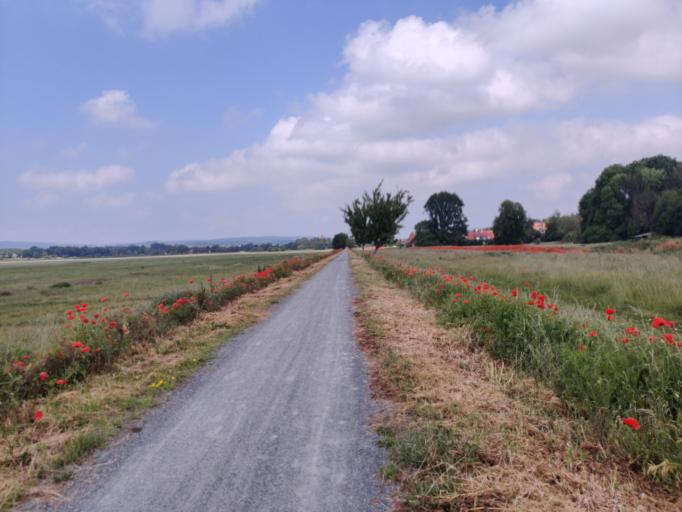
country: DE
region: Lower Saxony
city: Bad Salzdetfurth
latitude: 52.1084
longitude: 9.9984
